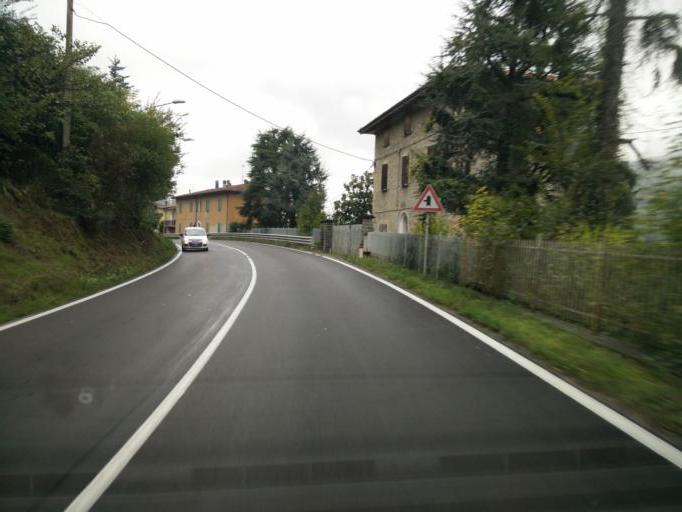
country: IT
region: Emilia-Romagna
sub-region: Provincia di Bologna
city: Marzabotto
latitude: 44.3659
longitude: 11.2132
